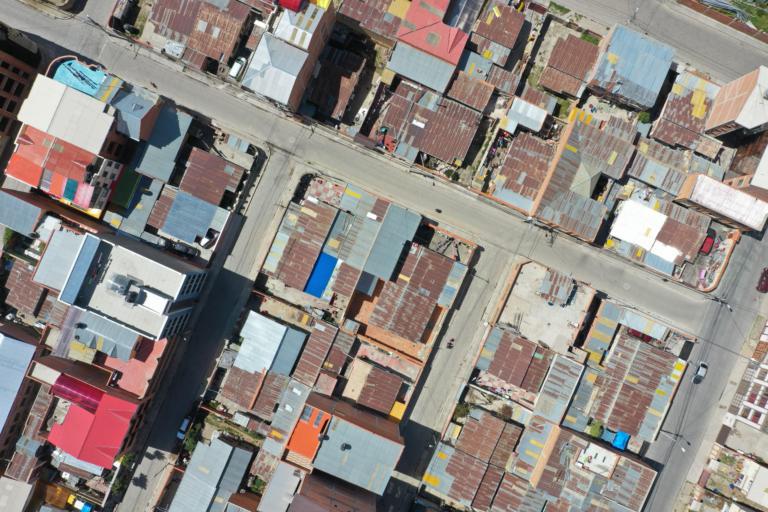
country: BO
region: La Paz
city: La Paz
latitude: -16.5209
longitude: -68.1547
